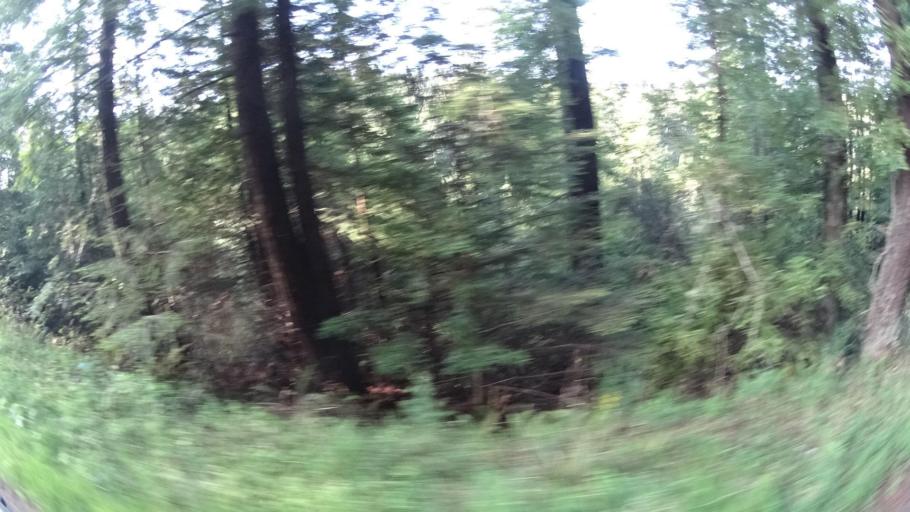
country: US
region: California
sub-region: Humboldt County
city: Bayside
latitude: 40.7550
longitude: -124.0464
